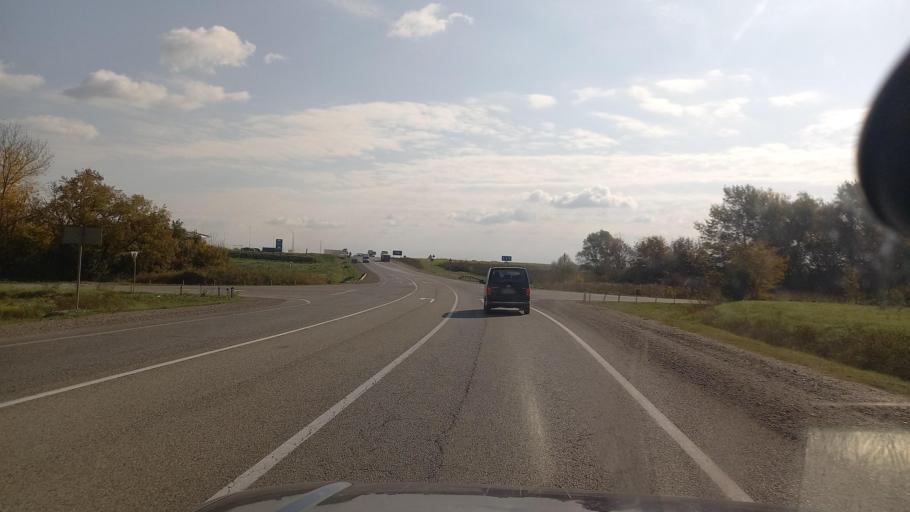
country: RU
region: Krasnodarskiy
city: Abinsk
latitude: 44.8748
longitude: 38.1111
